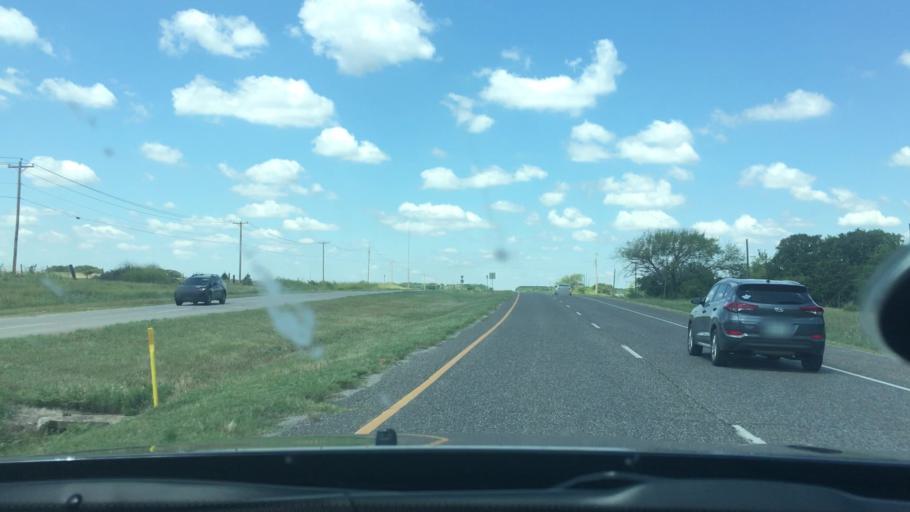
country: US
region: Oklahoma
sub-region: Carter County
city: Lone Grove
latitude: 34.1730
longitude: -97.2719
